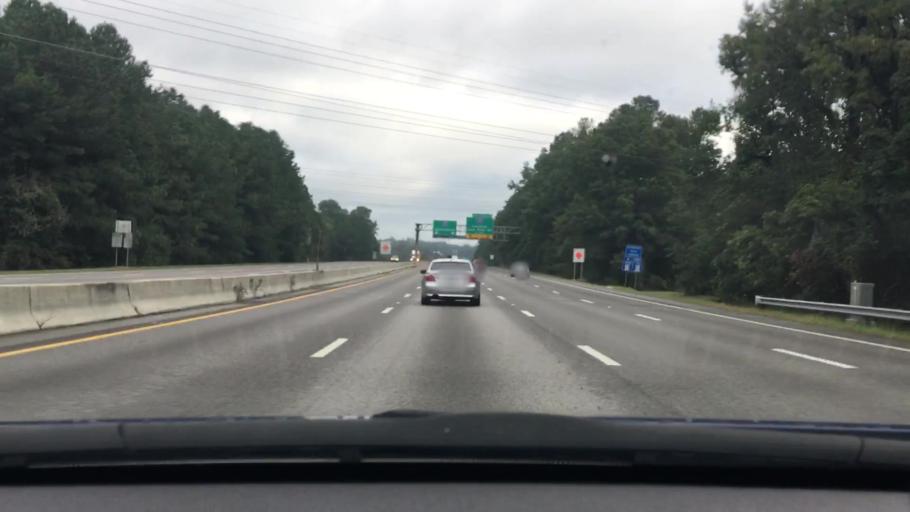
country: US
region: South Carolina
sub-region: Lexington County
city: Saint Andrews
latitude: 34.0164
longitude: -81.1070
